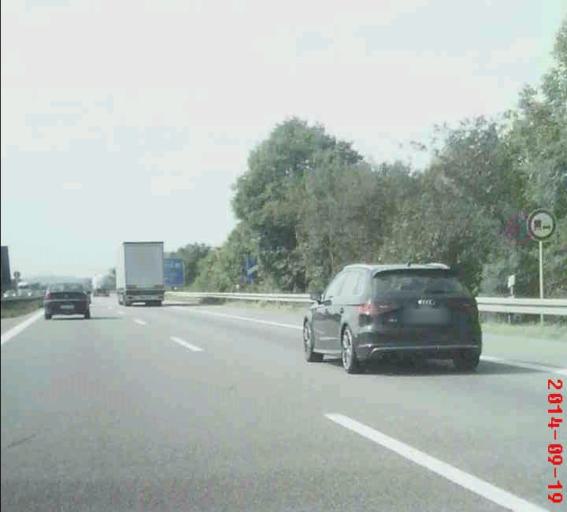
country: DE
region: Bavaria
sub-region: Upper Palatinate
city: Pentling
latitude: 48.9915
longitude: 12.0982
